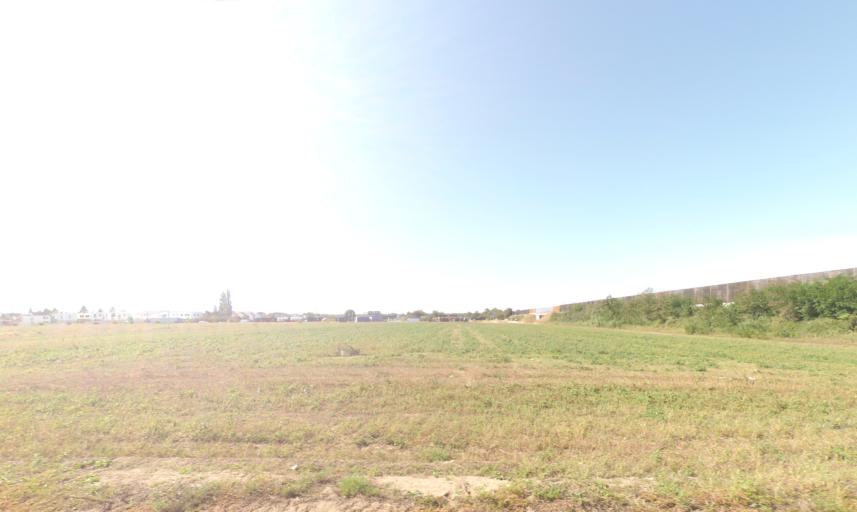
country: DE
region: Hesse
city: Lampertheim
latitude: 49.5528
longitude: 8.4509
